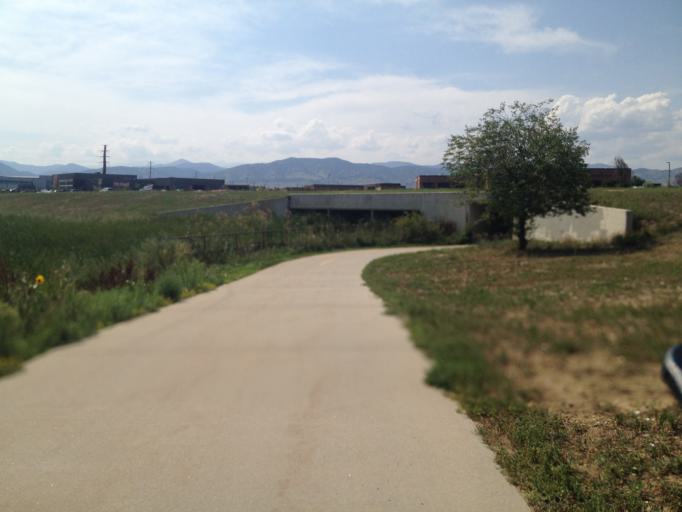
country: US
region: Colorado
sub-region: Boulder County
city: Boulder
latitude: 40.0234
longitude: -105.2311
